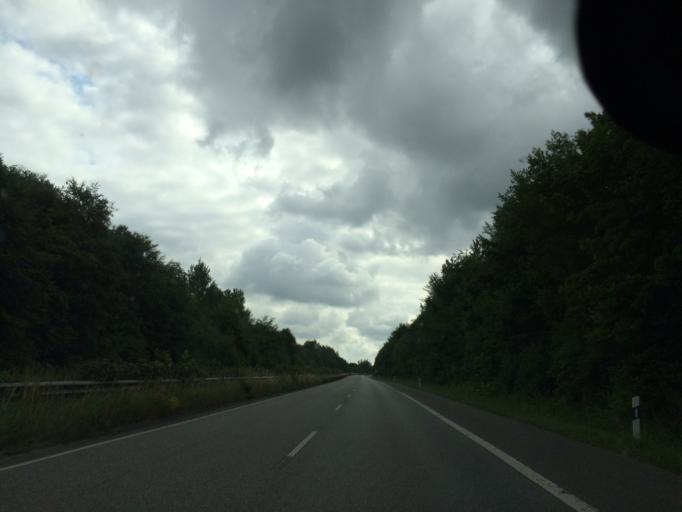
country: DE
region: Schleswig-Holstein
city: Kronshagen
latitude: 54.3520
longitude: 10.1075
